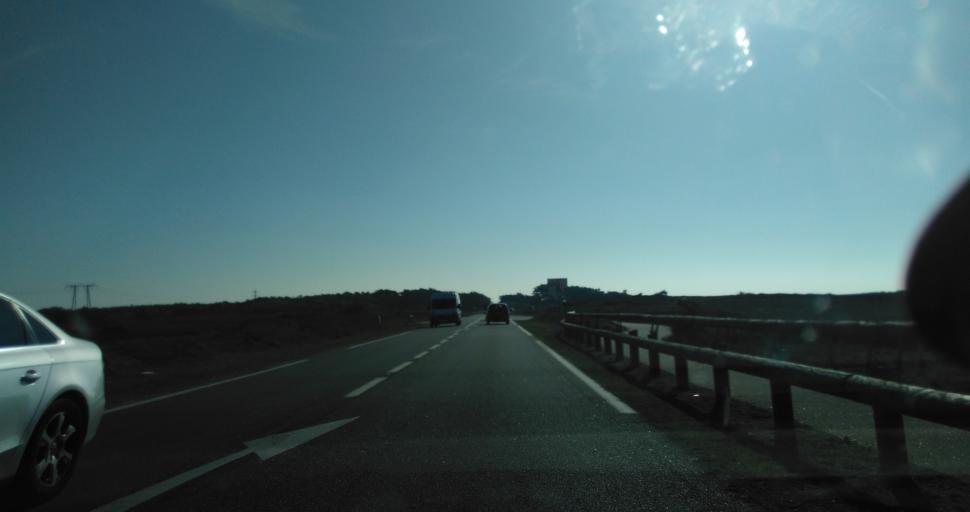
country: FR
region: Brittany
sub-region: Departement du Morbihan
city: Plouharnel
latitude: 47.5796
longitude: -3.1349
